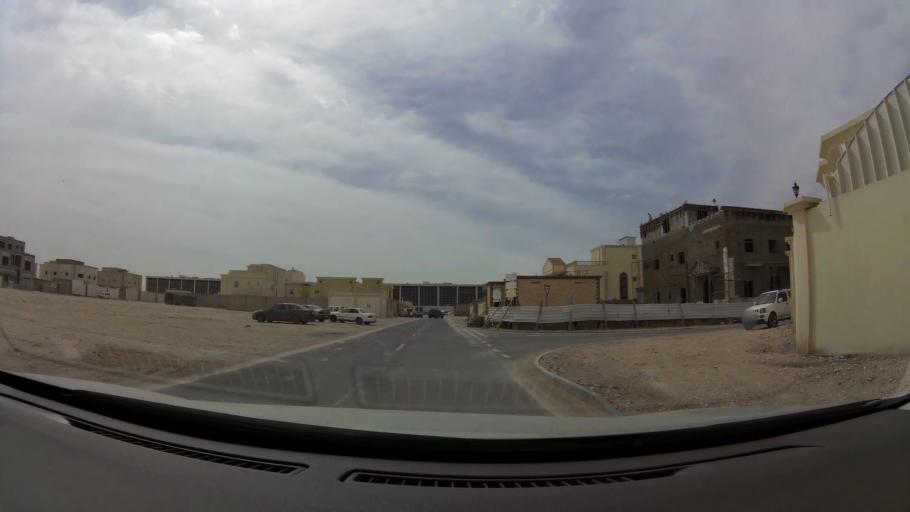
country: QA
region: Al Wakrah
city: Al Wukayr
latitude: 25.1981
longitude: 51.4594
